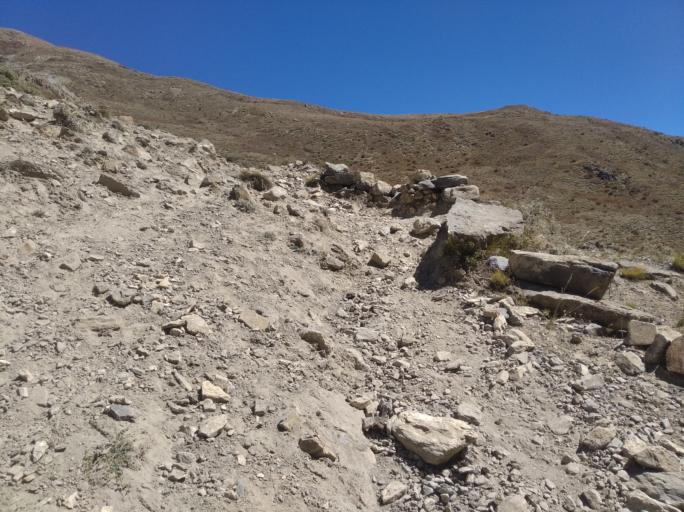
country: NP
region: Western Region
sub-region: Dhawalagiri Zone
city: Jomsom
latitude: 28.8393
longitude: 83.3653
